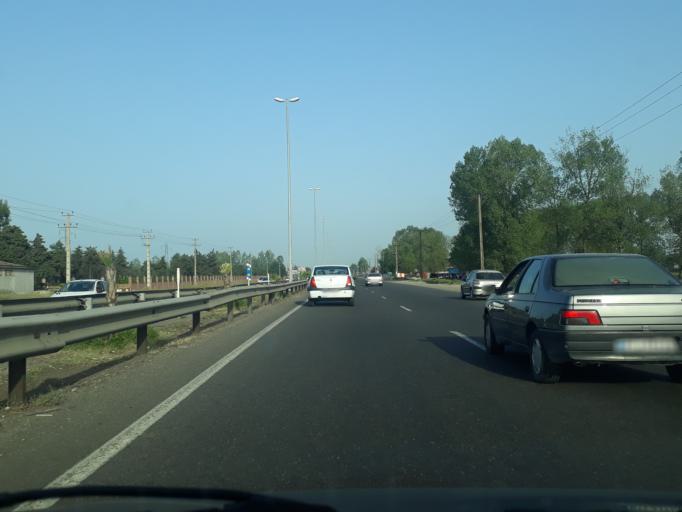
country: IR
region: Gilan
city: Bandar-e Anzali
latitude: 37.4608
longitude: 49.5726
